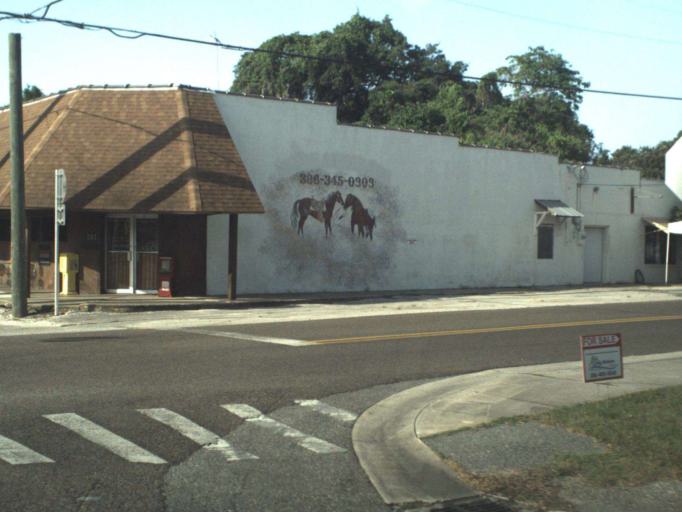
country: US
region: Florida
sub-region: Volusia County
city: Oak Hill
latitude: 28.8640
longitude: -80.8514
